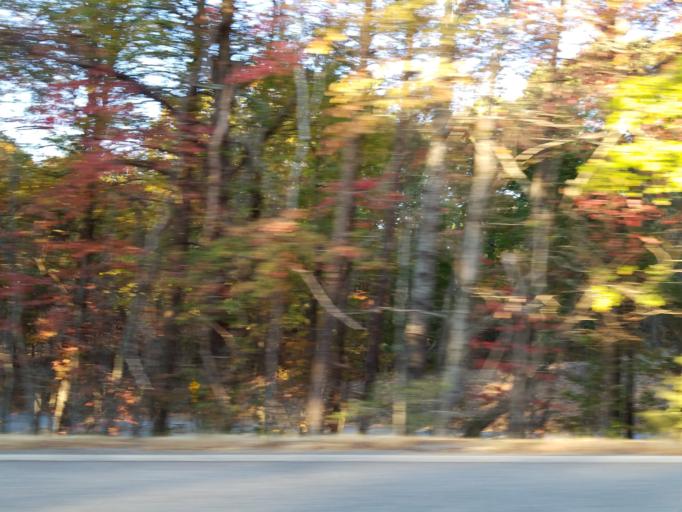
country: US
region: Georgia
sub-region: Dawson County
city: Dawsonville
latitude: 34.5469
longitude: -84.1221
